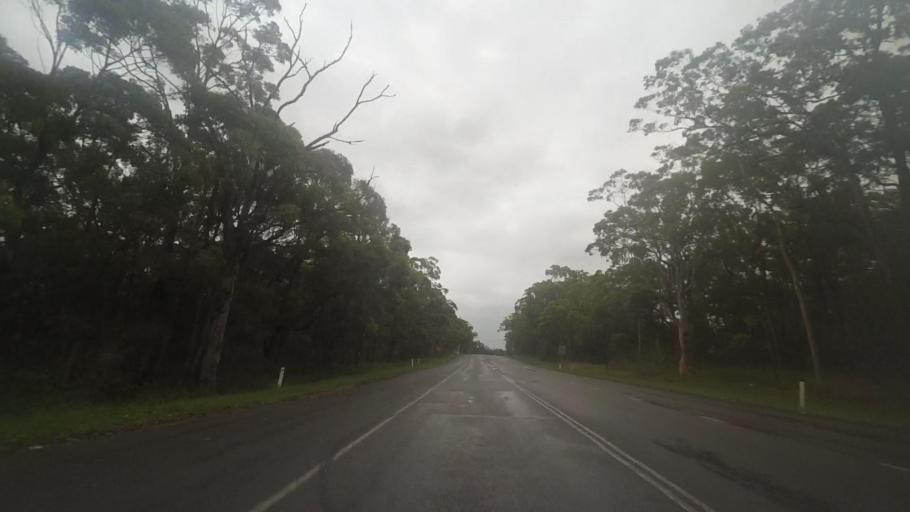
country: AU
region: New South Wales
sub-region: Port Stephens Shire
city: Medowie
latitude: -32.6520
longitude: 151.9388
